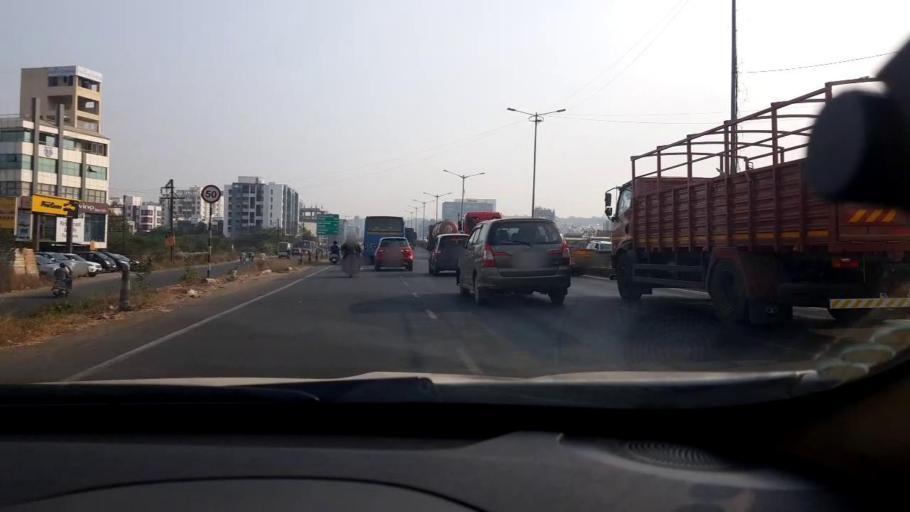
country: IN
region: Maharashtra
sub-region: Pune Division
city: Pimpri
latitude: 18.5636
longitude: 73.7678
